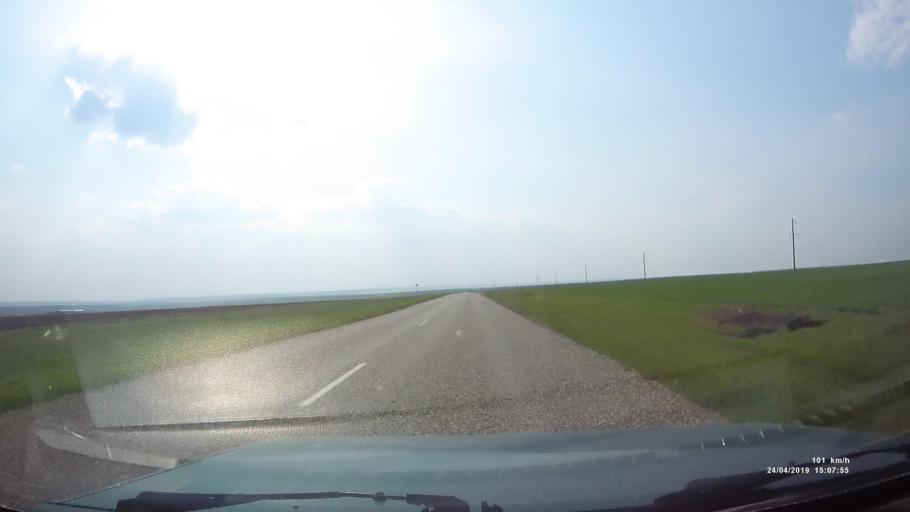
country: RU
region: Rostov
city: Remontnoye
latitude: 46.5599
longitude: 43.3941
